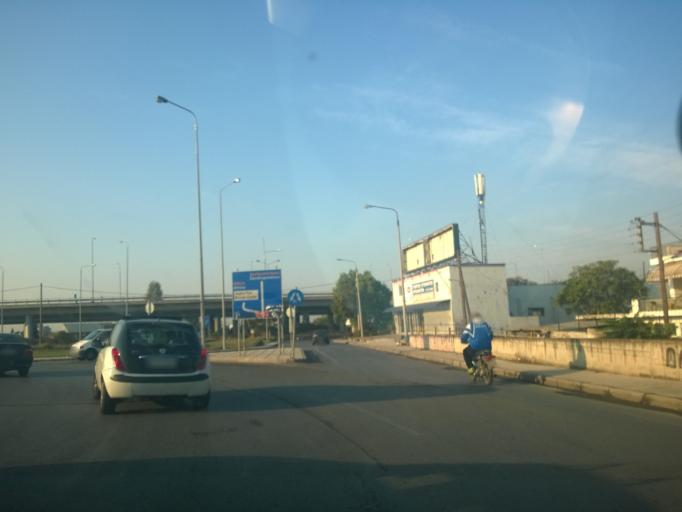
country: GR
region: Central Macedonia
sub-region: Nomos Thessalonikis
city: Menemeni
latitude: 40.6546
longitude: 22.9002
